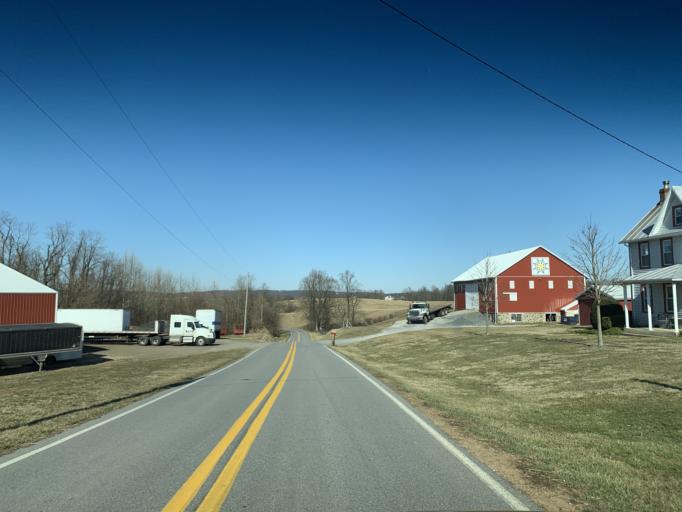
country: US
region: Maryland
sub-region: Carroll County
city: Westminster
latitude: 39.6399
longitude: -76.9661
